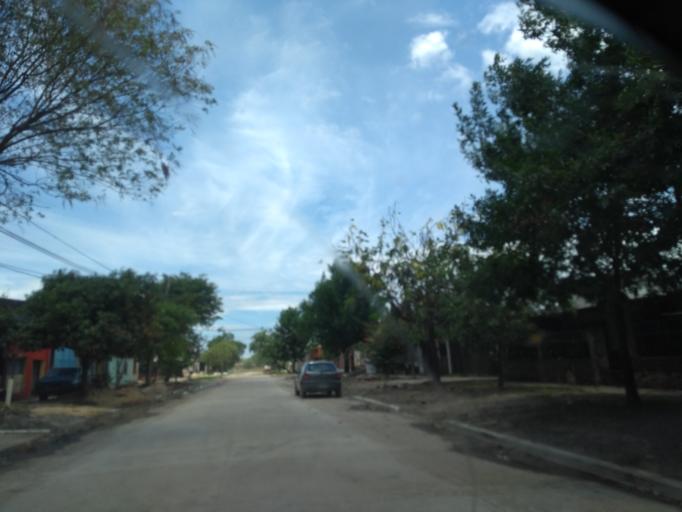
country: AR
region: Chaco
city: Resistencia
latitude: -27.4721
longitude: -58.9688
